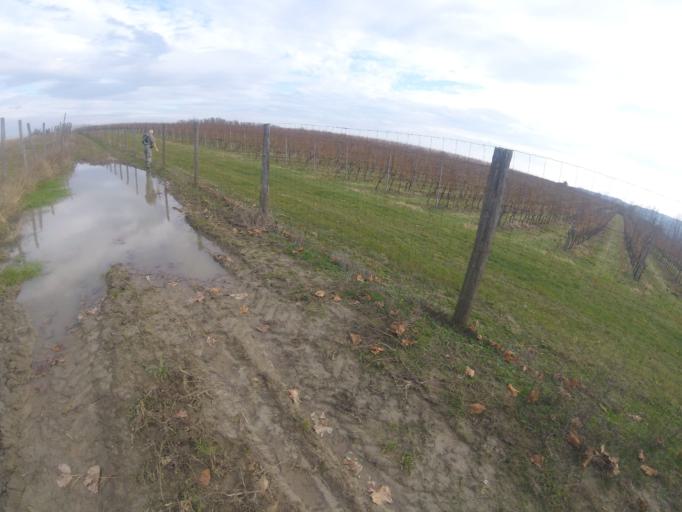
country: HU
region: Tolna
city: Bonyhad
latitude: 46.2426
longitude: 18.5946
